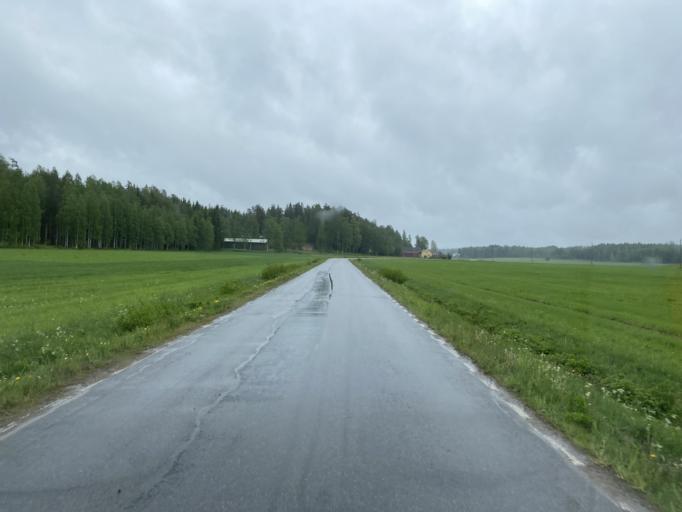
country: FI
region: Haeme
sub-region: Forssa
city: Humppila
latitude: 61.0497
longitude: 23.3632
